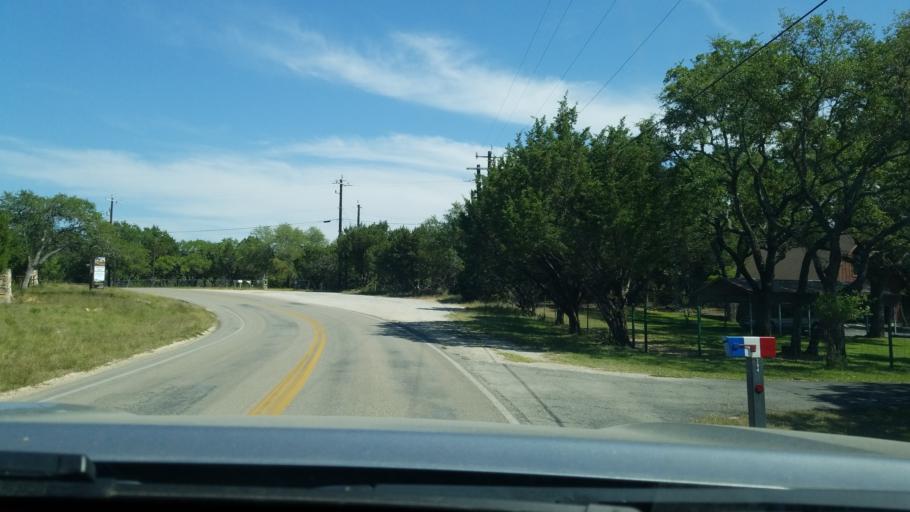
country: US
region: Texas
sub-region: Comal County
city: Bulverde
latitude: 29.7596
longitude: -98.5077
